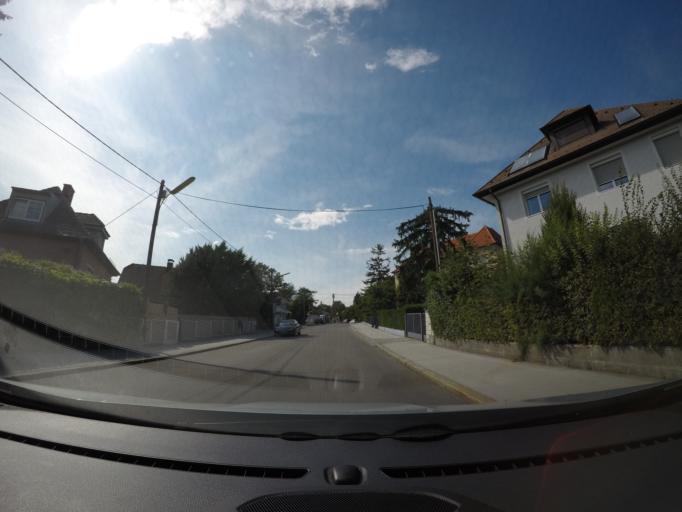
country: AT
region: Lower Austria
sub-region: Politischer Bezirk Modling
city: Perchtoldsdorf
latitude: 48.2041
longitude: 16.2697
